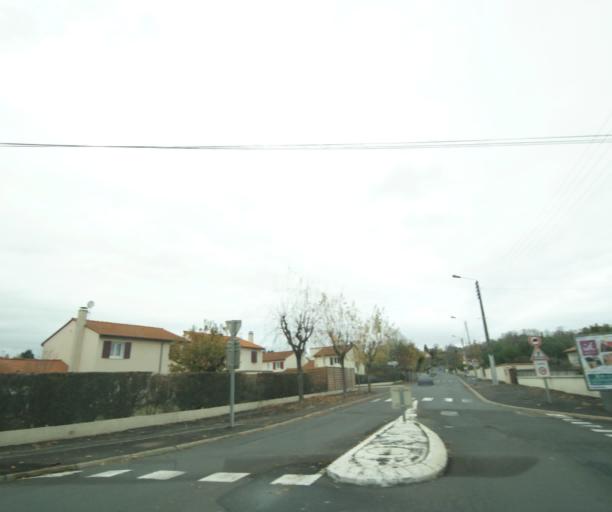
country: FR
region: Auvergne
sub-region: Departement du Puy-de-Dome
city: Pont-du-Chateau
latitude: 45.7920
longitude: 3.2398
